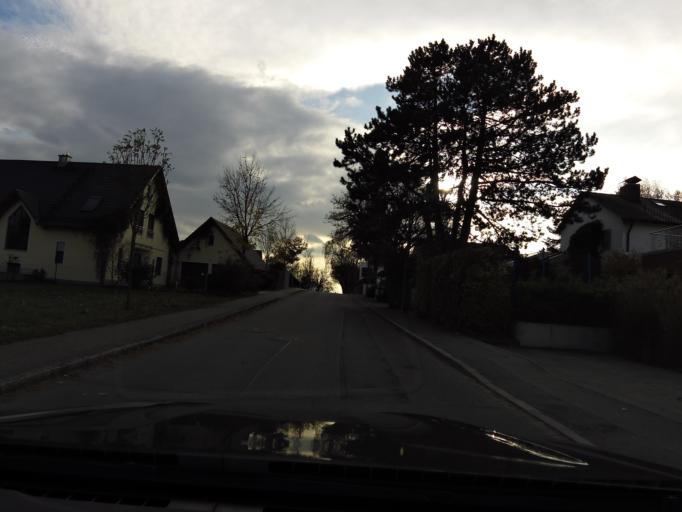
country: DE
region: Bavaria
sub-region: Lower Bavaria
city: Landshut
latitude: 48.5218
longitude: 12.1620
